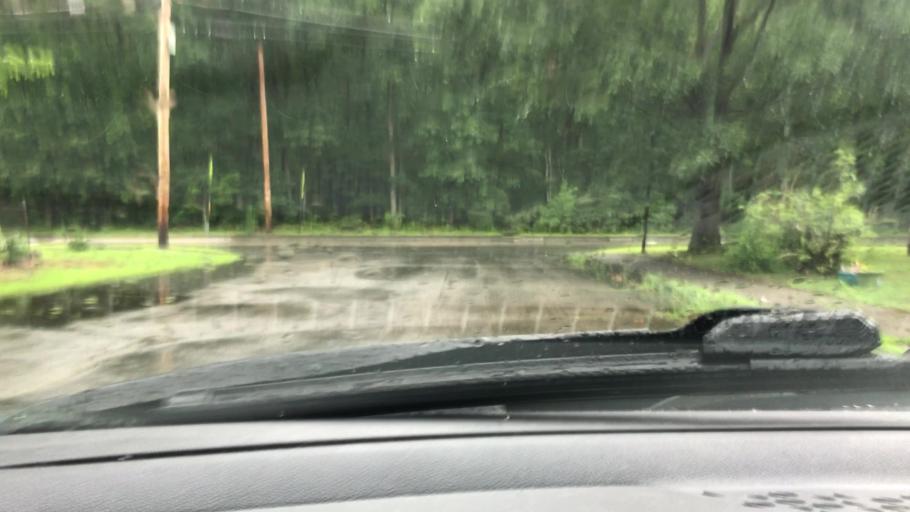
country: US
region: New Hampshire
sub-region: Merrimack County
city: East Concord
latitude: 43.2616
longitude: -71.5829
